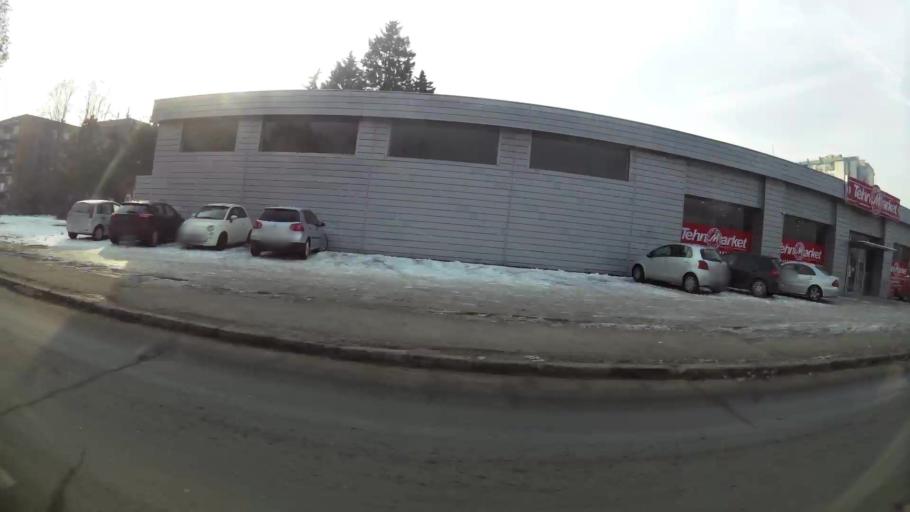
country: MK
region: Butel
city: Butel
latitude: 42.0250
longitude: 21.4427
